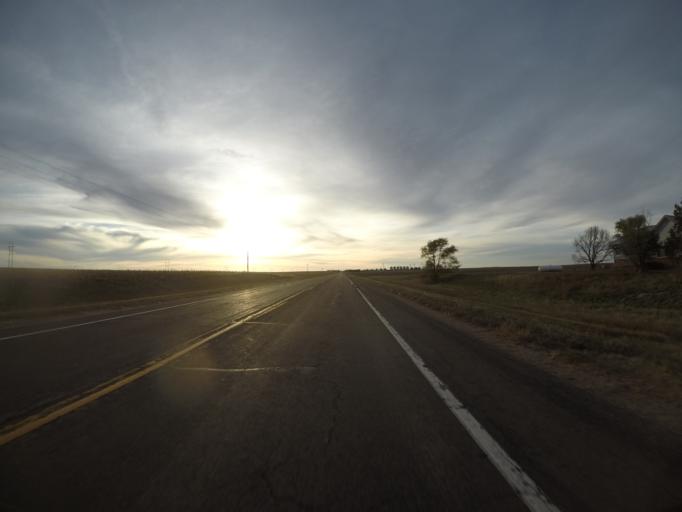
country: US
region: Colorado
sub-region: Washington County
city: Akron
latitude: 39.7415
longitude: -103.1989
